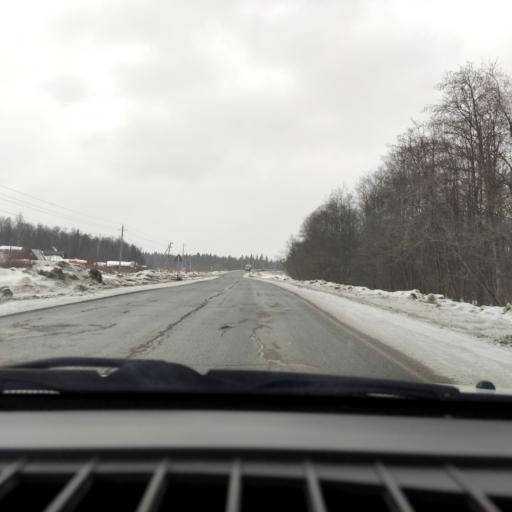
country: RU
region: Perm
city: Overyata
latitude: 58.0998
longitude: 55.8111
